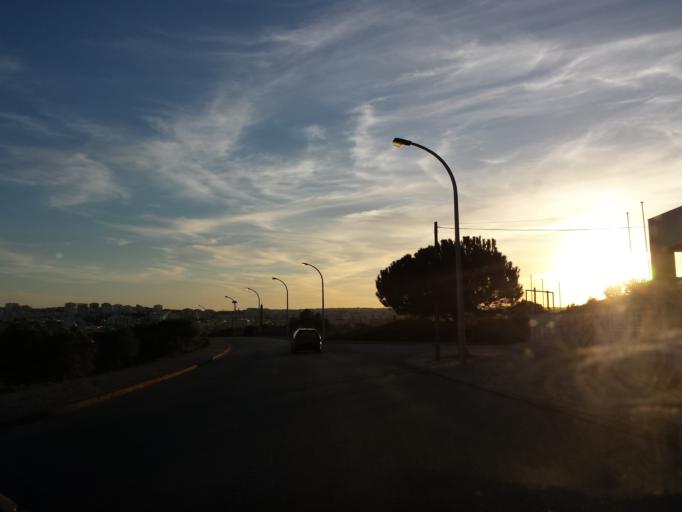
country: PT
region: Faro
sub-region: Lagos
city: Lagos
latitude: 37.1148
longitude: -8.6704
